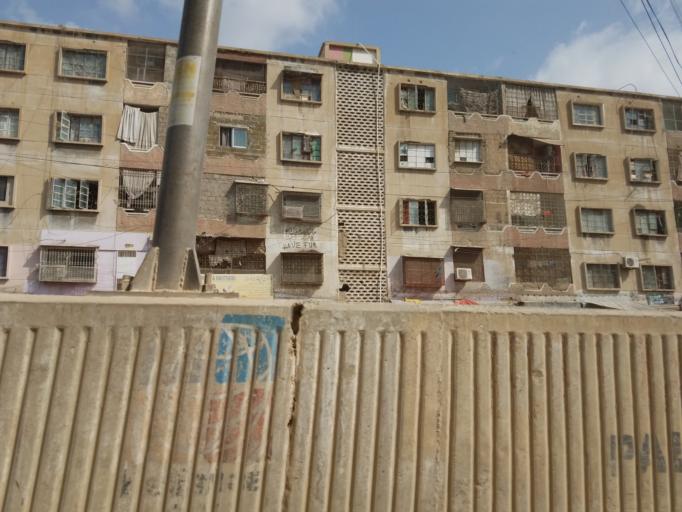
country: PK
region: Sindh
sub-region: Karachi District
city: Karachi
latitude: 24.9126
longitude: 67.0507
